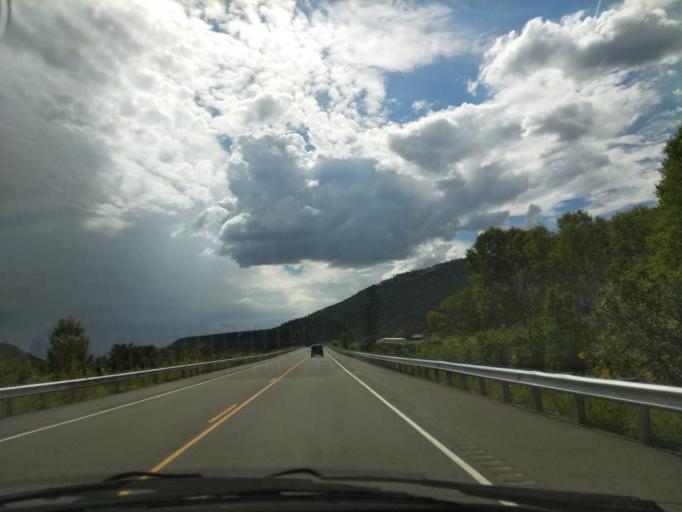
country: US
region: Colorado
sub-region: Delta County
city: Paonia
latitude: 38.9152
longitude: -107.5452
